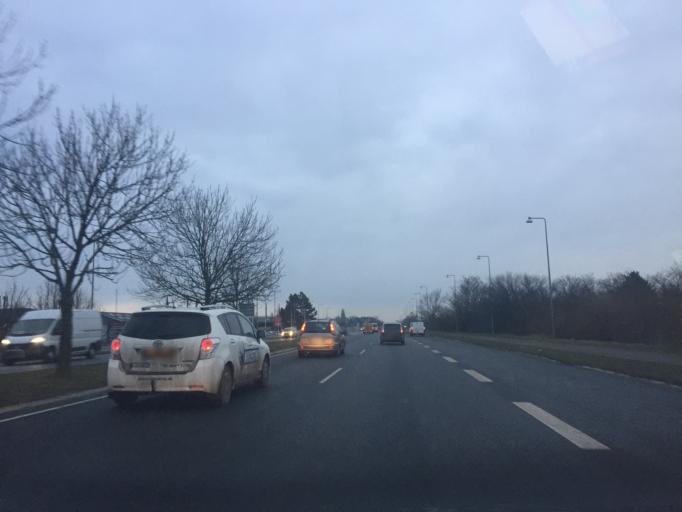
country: DK
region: Zealand
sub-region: Solrod Kommune
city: Solrod
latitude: 55.5000
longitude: 12.1962
